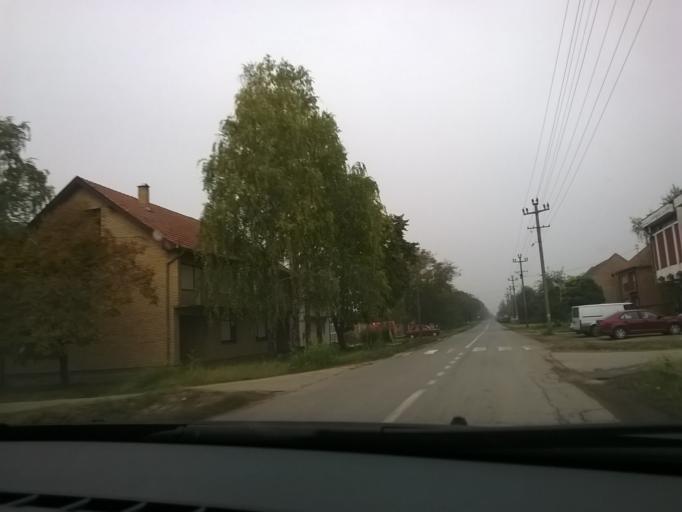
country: RS
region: Autonomna Pokrajina Vojvodina
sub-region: Juznobanatski Okrug
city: Kovin
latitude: 44.8809
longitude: 20.9697
